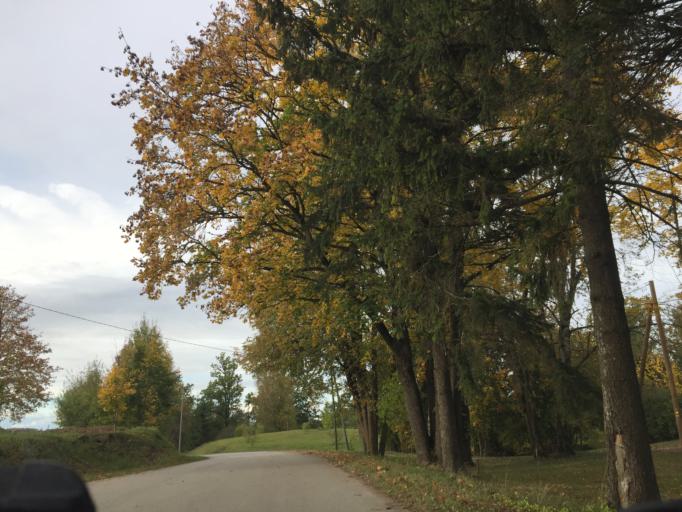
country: LV
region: Auces Novads
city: Auce
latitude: 56.5422
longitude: 22.9955
